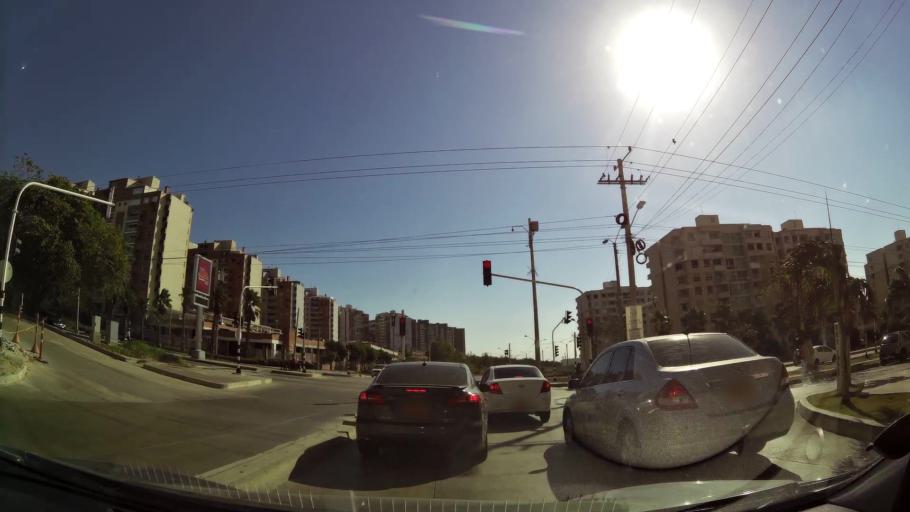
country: CO
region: Atlantico
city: Barranquilla
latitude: 11.0083
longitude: -74.8338
